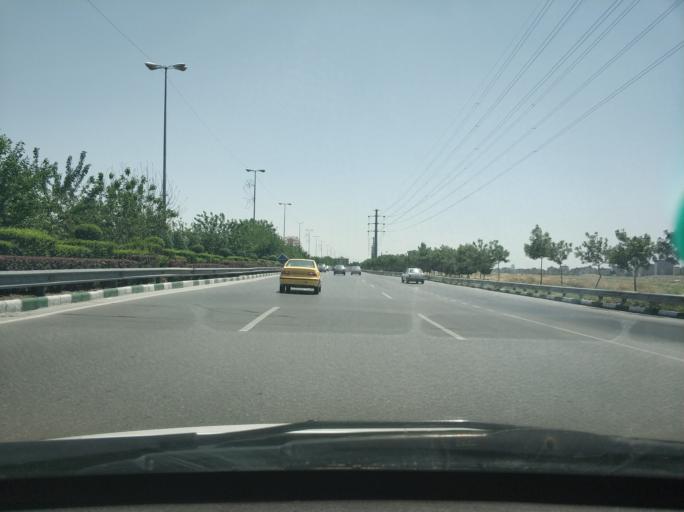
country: IR
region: Razavi Khorasan
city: Mashhad
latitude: 36.3465
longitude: 59.4869
